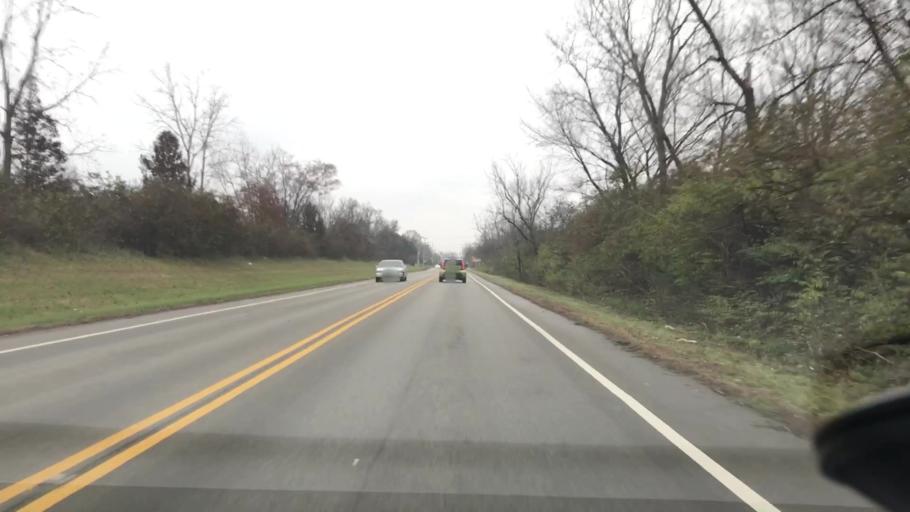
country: US
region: Ohio
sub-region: Franklin County
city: Upper Arlington
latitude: 40.0085
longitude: -83.1066
